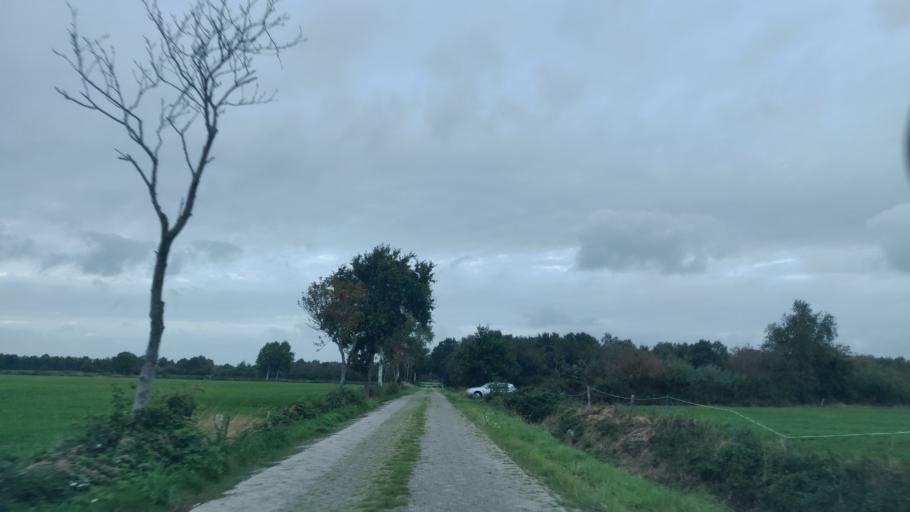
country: DE
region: Lower Saxony
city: Aurich
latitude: 53.5295
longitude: 7.4728
